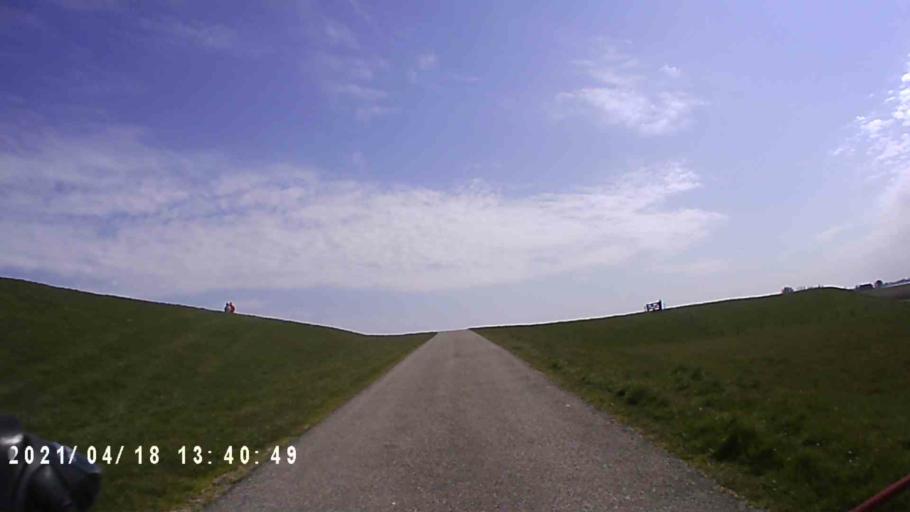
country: NL
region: Friesland
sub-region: Gemeente Dongeradeel
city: Anjum
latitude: 53.4006
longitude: 6.0990
